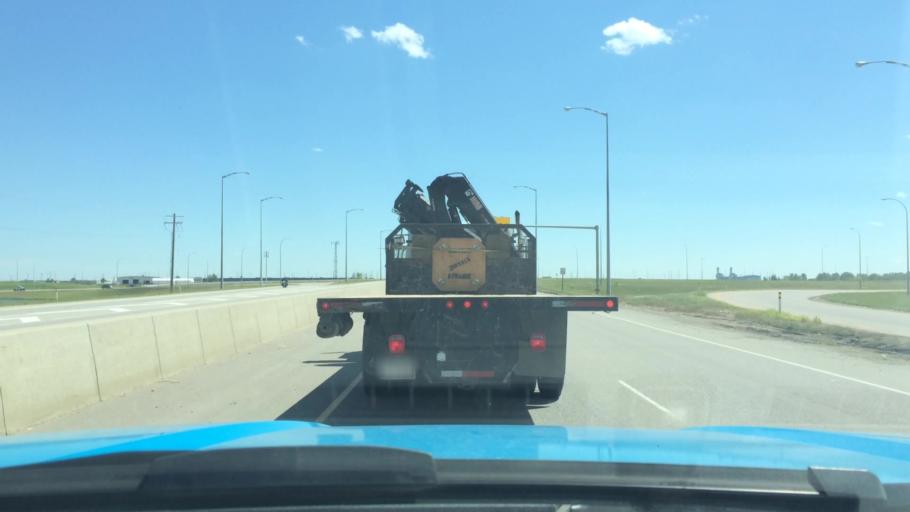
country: CA
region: Alberta
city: Chestermere
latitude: 50.9795
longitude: -113.9276
